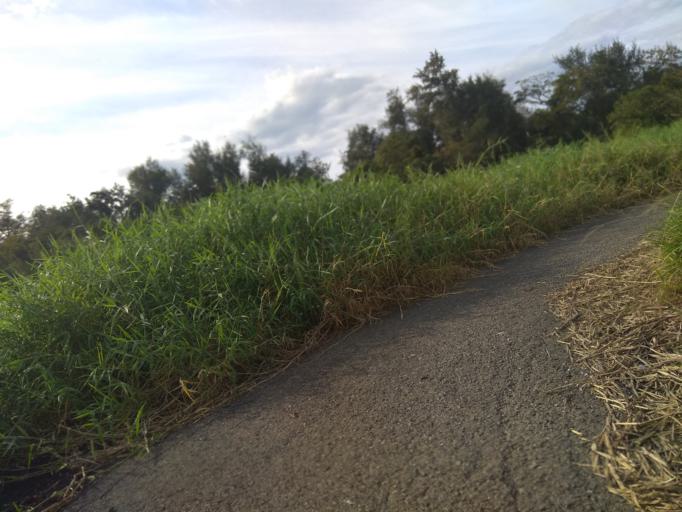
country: TW
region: Taiwan
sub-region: Hsinchu
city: Zhubei
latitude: 24.9558
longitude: 121.0028
